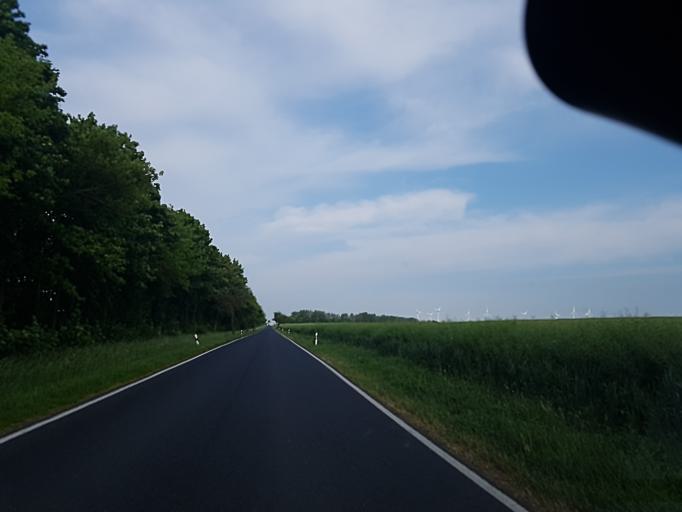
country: DE
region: Saxony-Anhalt
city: Zahna
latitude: 51.9725
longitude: 12.8464
